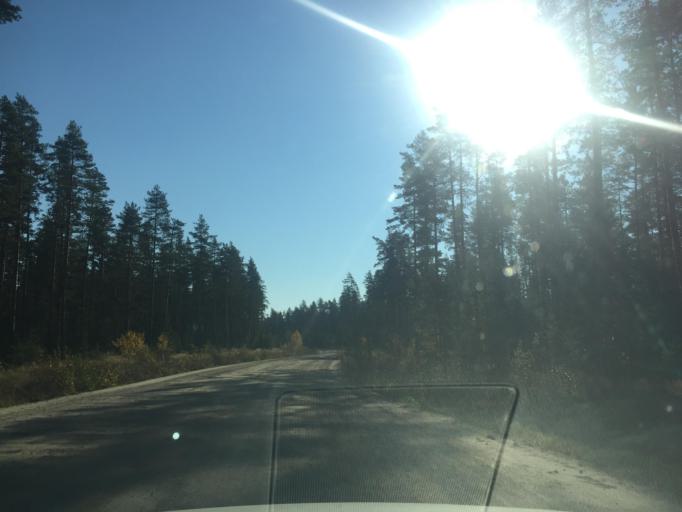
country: RU
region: Republic of Karelia
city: Lakhdenpokh'ya
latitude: 61.3859
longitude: 29.9611
